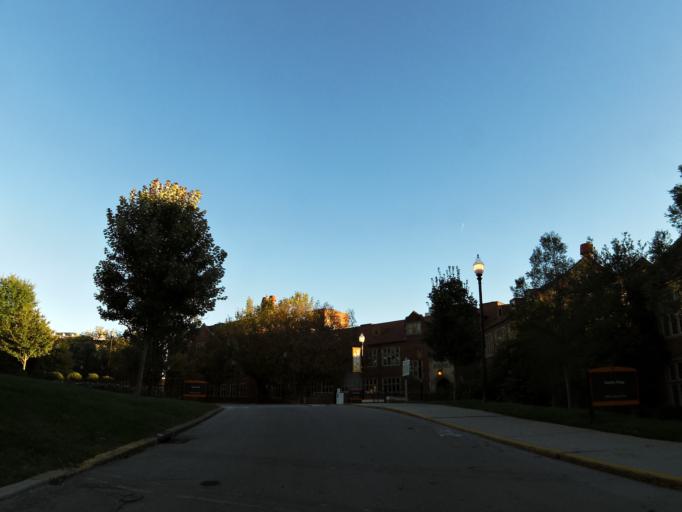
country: US
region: Tennessee
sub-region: Knox County
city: Knoxville
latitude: 35.9573
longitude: -83.9267
